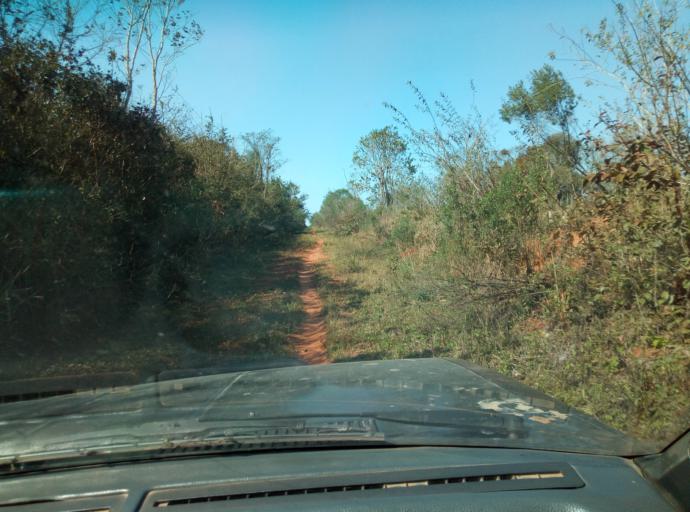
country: PY
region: Caaguazu
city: Doctor Cecilio Baez
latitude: -25.1793
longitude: -56.2180
